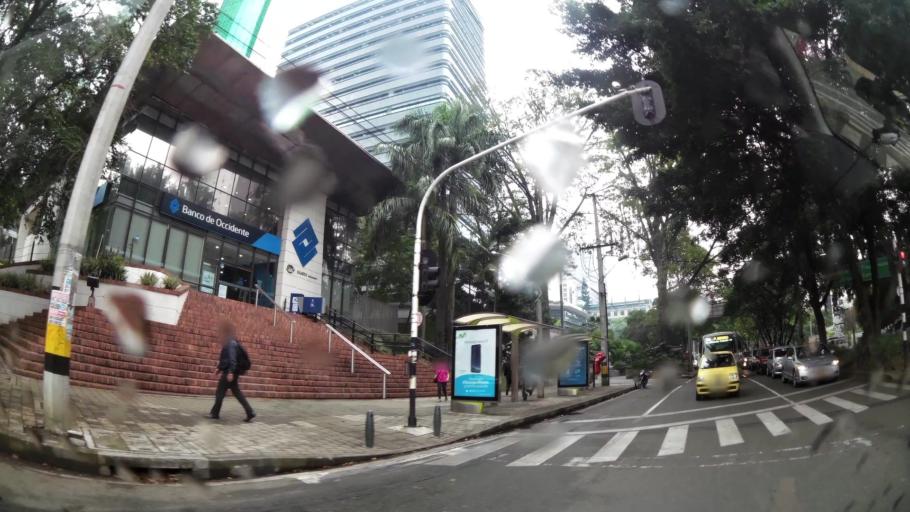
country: CO
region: Antioquia
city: Itagui
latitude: 6.2009
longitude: -75.5726
